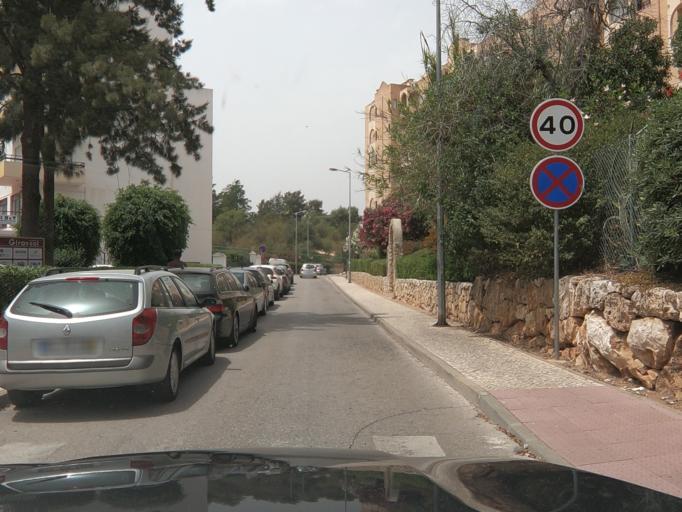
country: PT
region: Faro
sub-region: Portimao
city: Portimao
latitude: 37.1216
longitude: -8.5392
